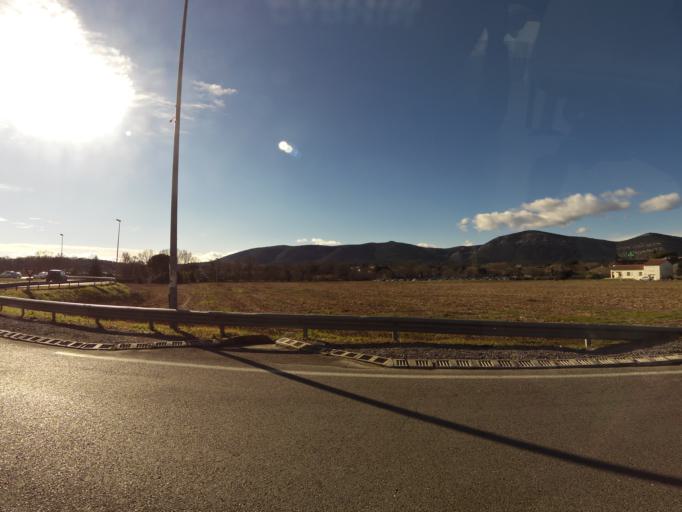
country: FR
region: Languedoc-Roussillon
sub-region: Departement du Gard
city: Quissac
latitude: 43.9065
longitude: 4.0049
